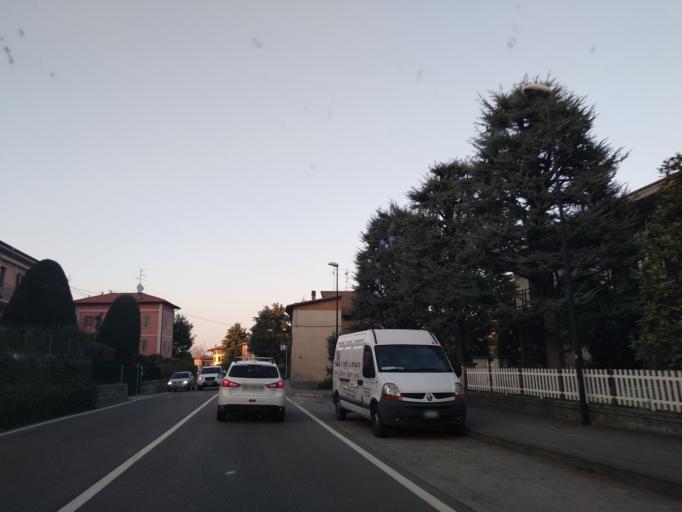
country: IT
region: Emilia-Romagna
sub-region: Provincia di Reggio Emilia
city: Vezzano sul Crostolo
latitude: 44.6049
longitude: 10.5484
